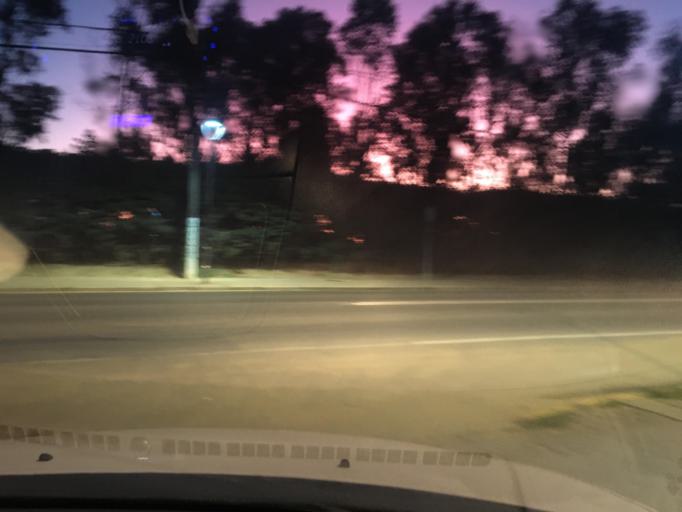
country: CL
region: Valparaiso
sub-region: San Antonio Province
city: El Tabo
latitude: -33.4383
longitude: -71.6843
